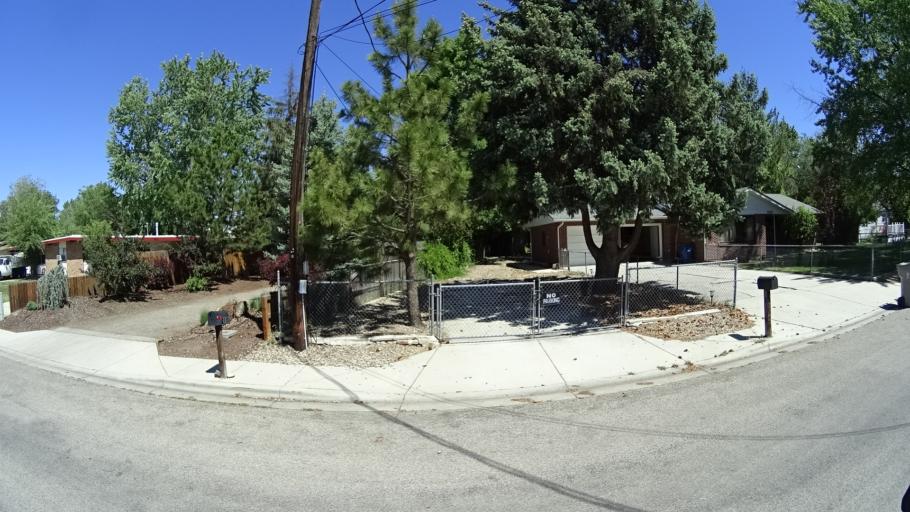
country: US
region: Idaho
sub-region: Ada County
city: Garden City
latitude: 43.5825
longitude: -116.2423
